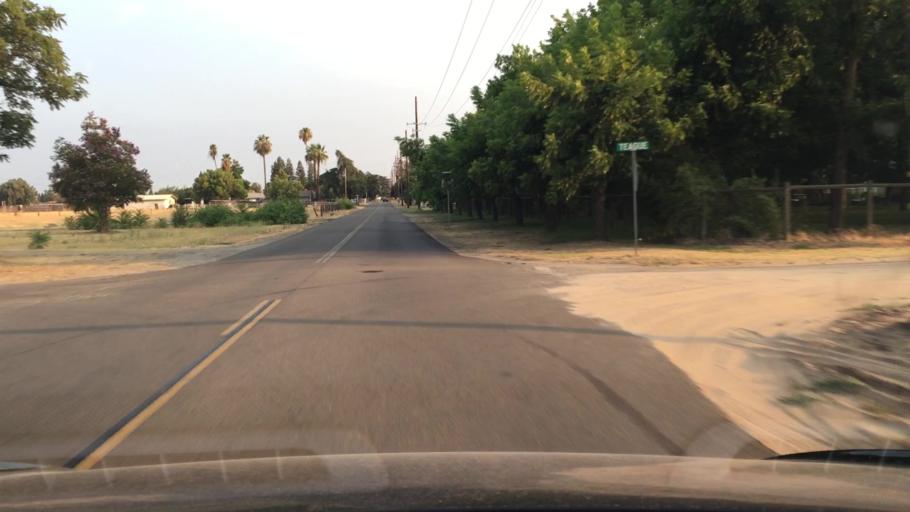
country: US
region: California
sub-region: Fresno County
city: Clovis
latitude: 36.8594
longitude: -119.6931
